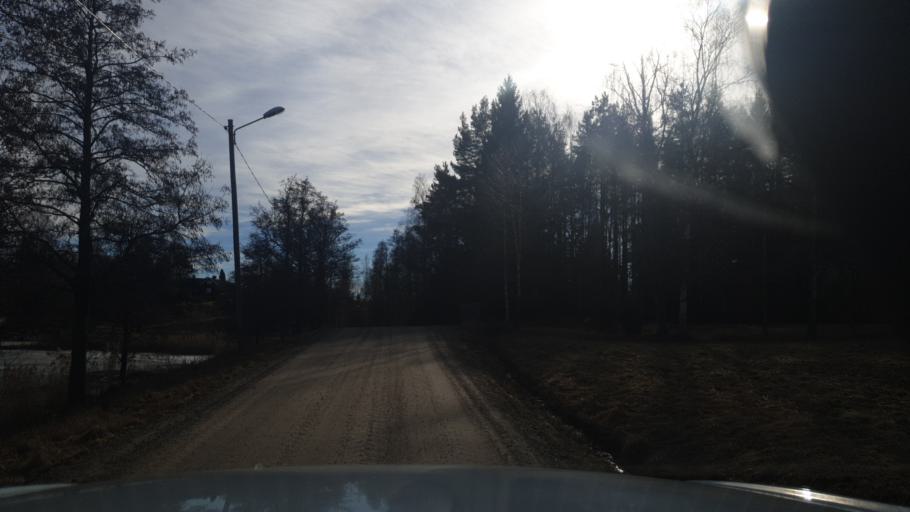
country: SE
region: Vaermland
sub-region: Karlstads Kommun
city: Edsvalla
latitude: 59.6061
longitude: 12.9173
